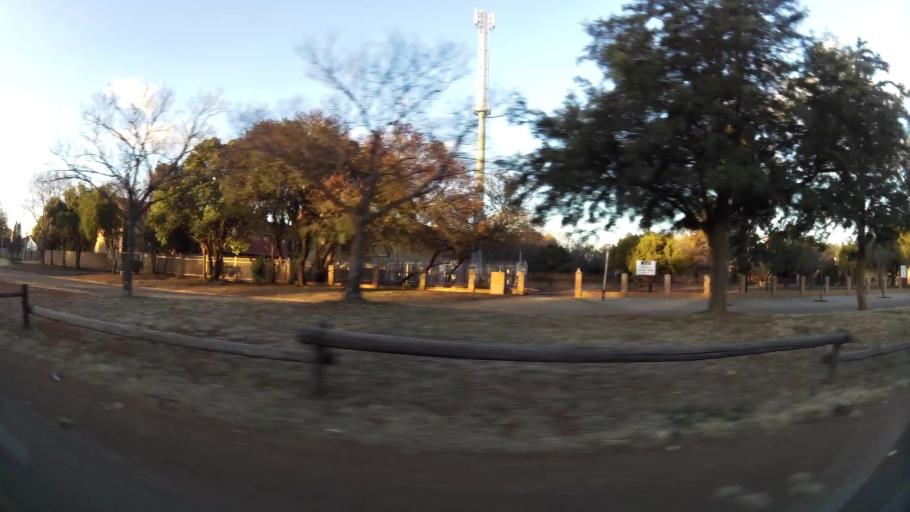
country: ZA
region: North-West
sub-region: Dr Kenneth Kaunda District Municipality
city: Potchefstroom
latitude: -26.7182
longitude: 27.1140
